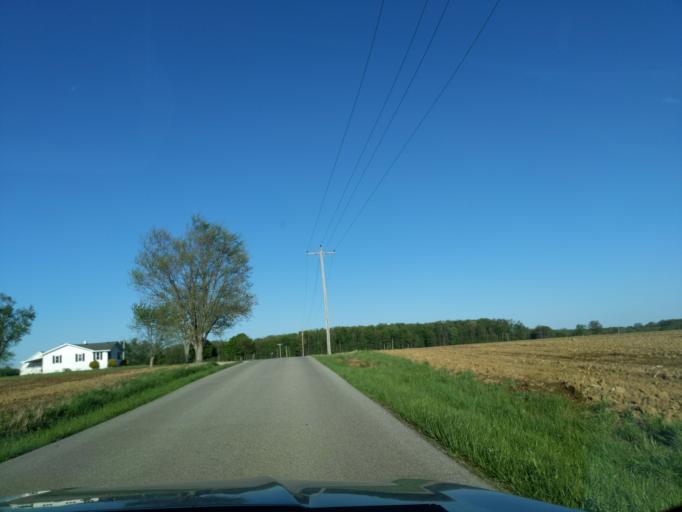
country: US
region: Indiana
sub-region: Decatur County
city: Westport
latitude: 39.1981
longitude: -85.5514
